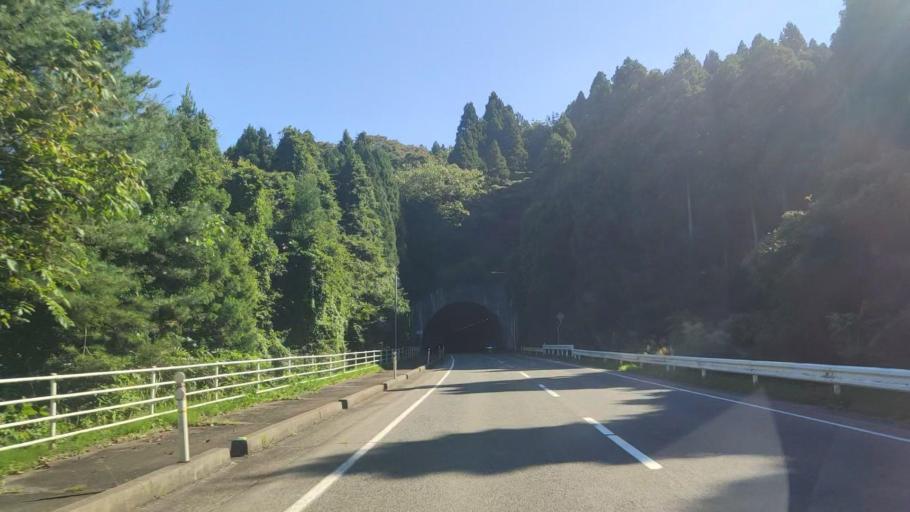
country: JP
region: Ishikawa
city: Nanao
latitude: 37.3853
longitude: 137.2331
